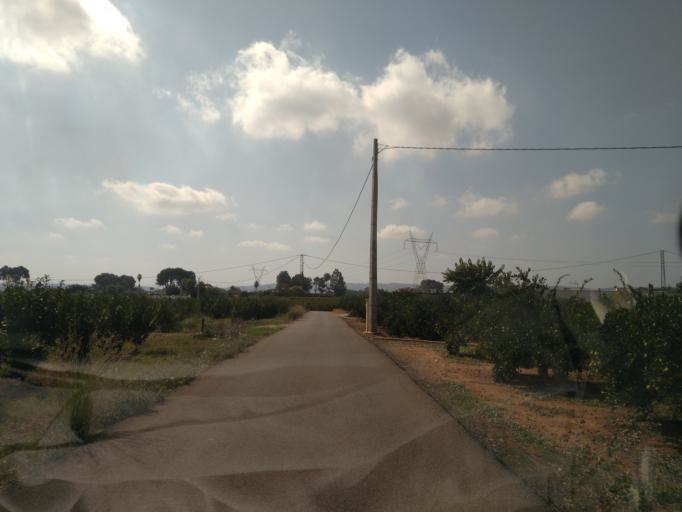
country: ES
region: Valencia
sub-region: Provincia de Valencia
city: Benimodo
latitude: 39.1816
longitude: -0.5486
